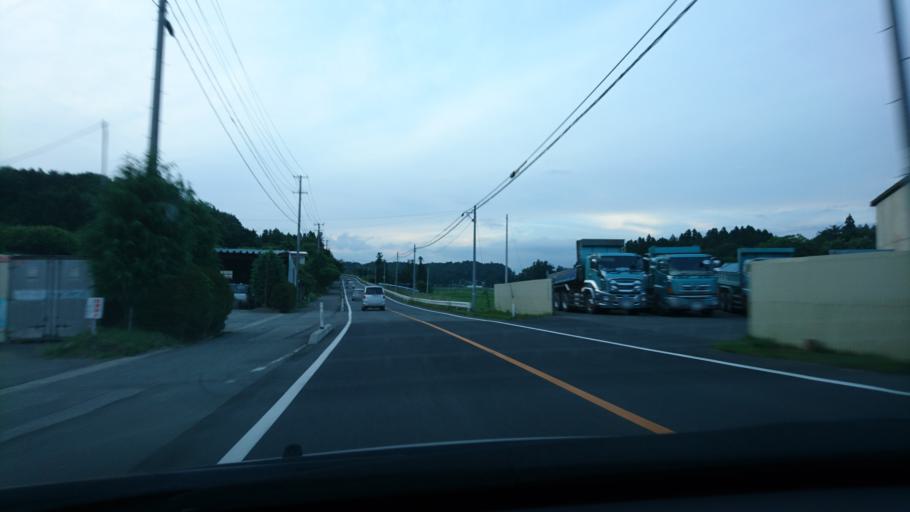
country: JP
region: Miyagi
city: Furukawa
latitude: 38.7639
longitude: 141.0039
